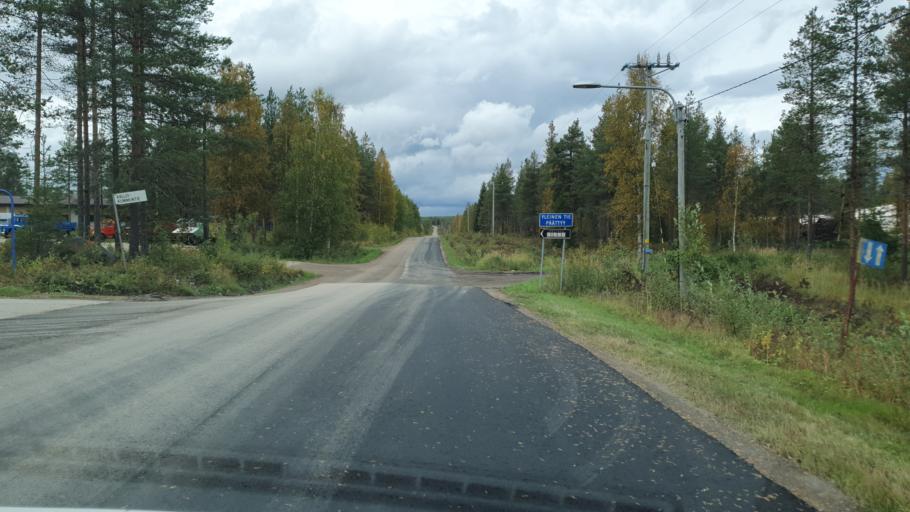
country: FI
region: Lapland
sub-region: Rovaniemi
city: Rovaniemi
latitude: 66.4265
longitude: 25.3970
